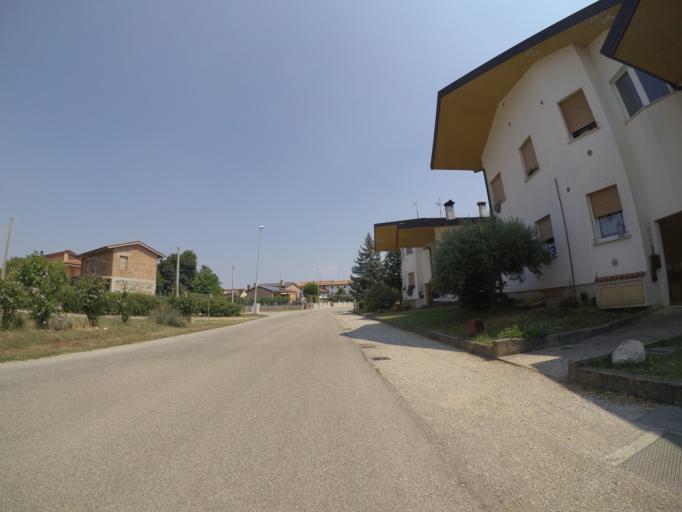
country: IT
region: Friuli Venezia Giulia
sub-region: Provincia di Udine
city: Basiliano-Vissandone
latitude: 46.0266
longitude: 13.1070
